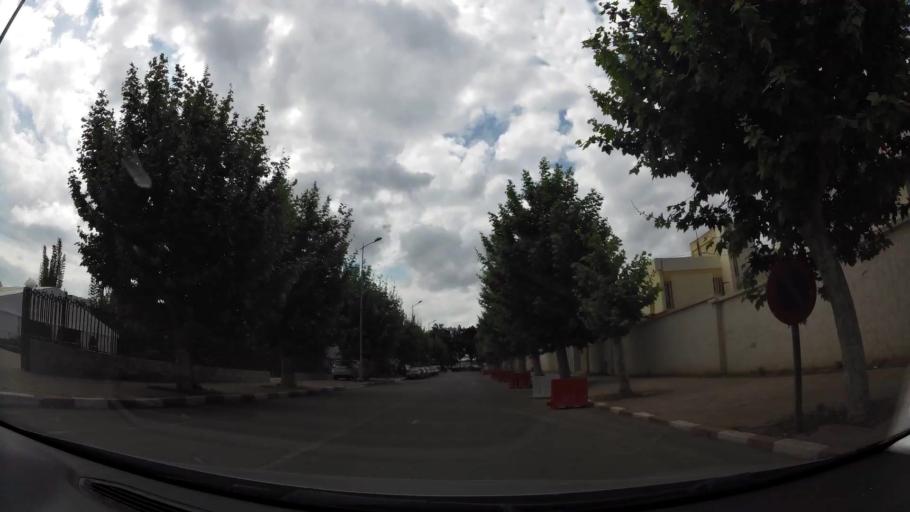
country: MA
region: Gharb-Chrarda-Beni Hssen
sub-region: Kenitra Province
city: Kenitra
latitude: 34.2539
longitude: -6.5858
